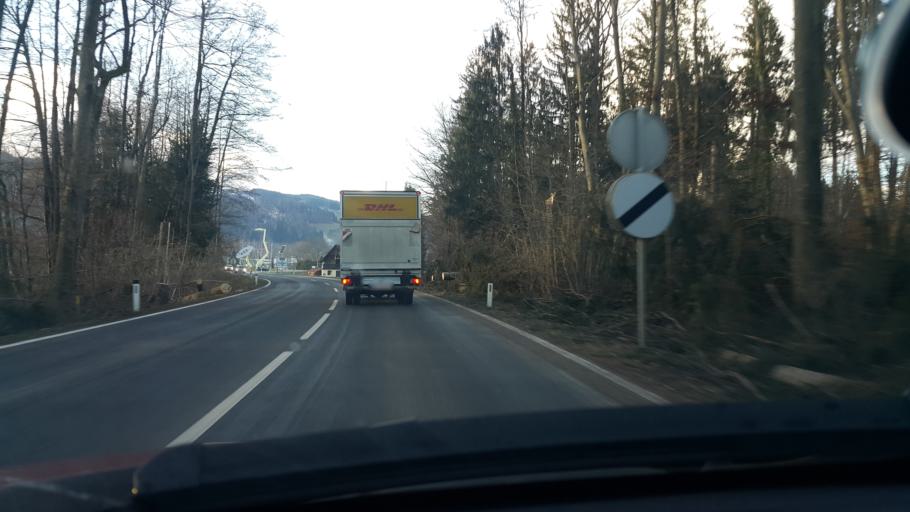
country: AT
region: Styria
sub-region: Politischer Bezirk Deutschlandsberg
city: Hollenegg
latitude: 46.7991
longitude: 15.2234
